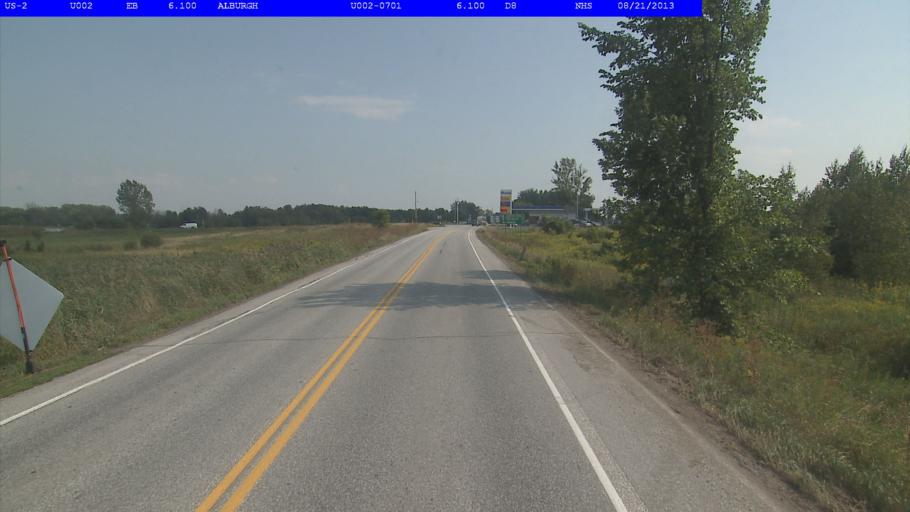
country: US
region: New York
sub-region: Clinton County
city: Rouses Point
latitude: 44.9611
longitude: -73.2790
